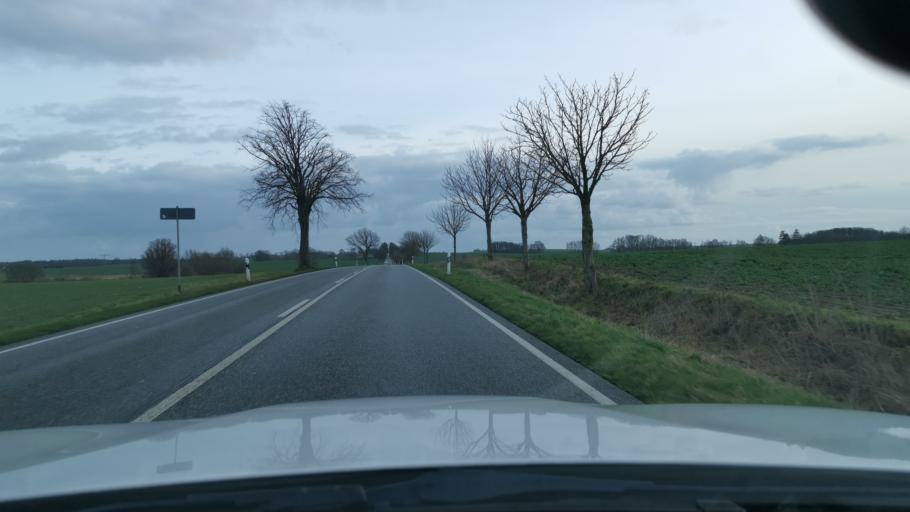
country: DE
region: Mecklenburg-Vorpommern
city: Laage
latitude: 53.9691
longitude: 12.2888
